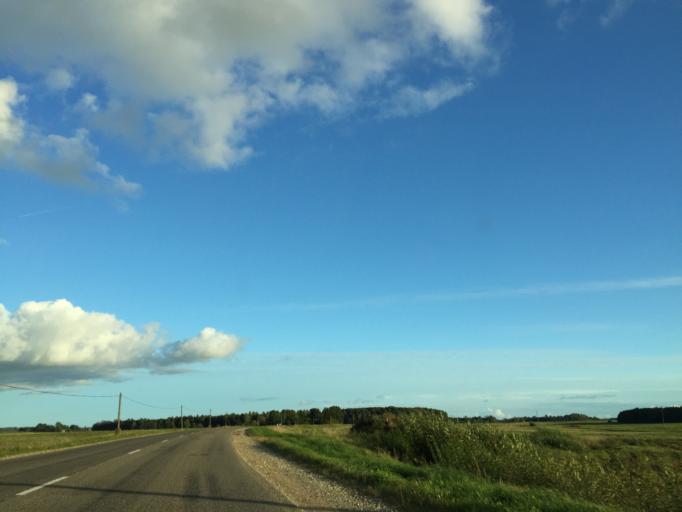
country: LV
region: Saldus Rajons
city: Saldus
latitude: 56.7491
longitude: 22.3743
